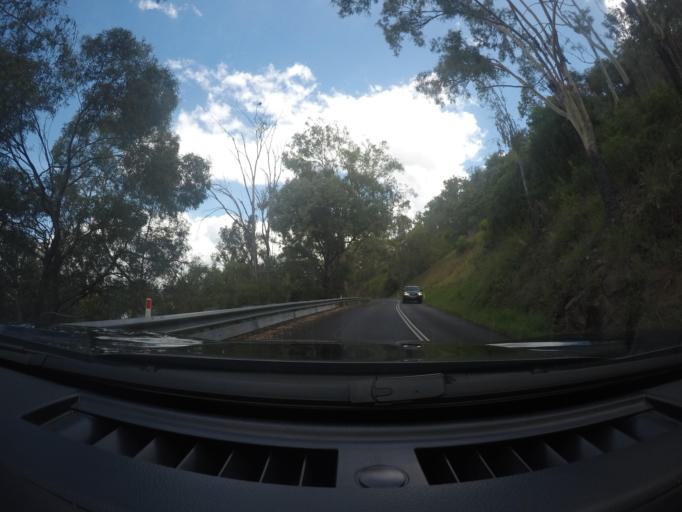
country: AU
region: Queensland
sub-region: Moreton Bay
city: Woodford
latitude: -27.0959
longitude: 152.5624
